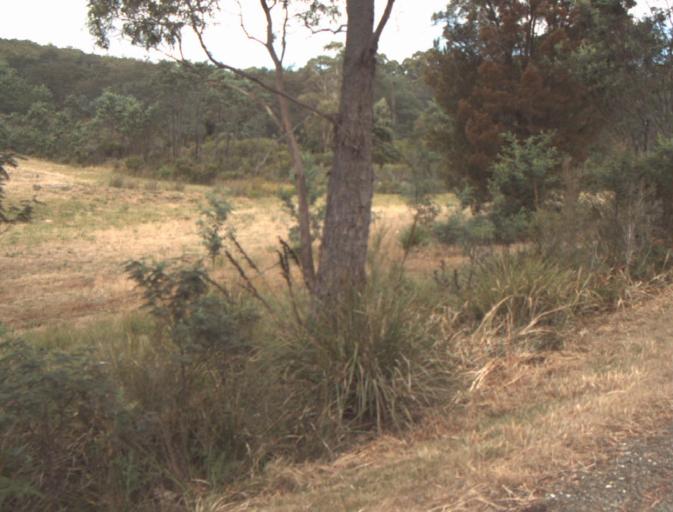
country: AU
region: Tasmania
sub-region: Launceston
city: Mayfield
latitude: -41.2179
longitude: 147.0505
